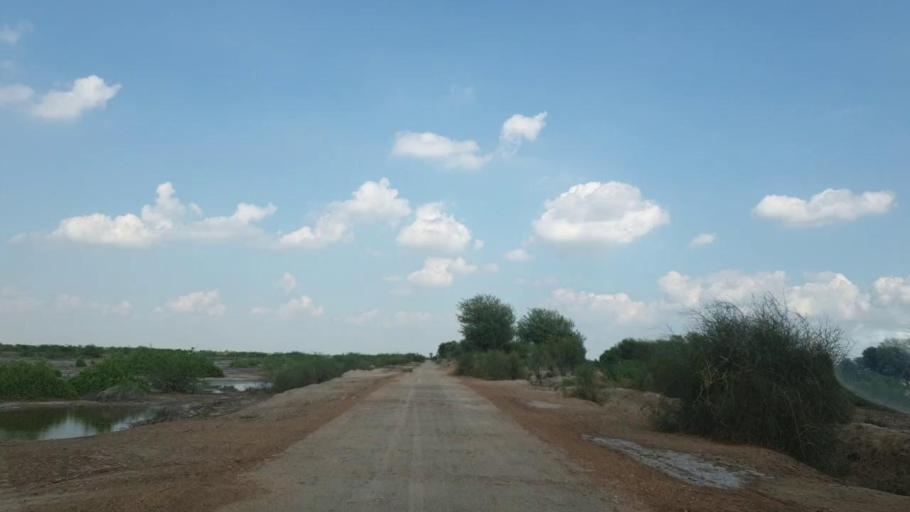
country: PK
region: Sindh
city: Pithoro
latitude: 25.6055
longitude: 69.3632
